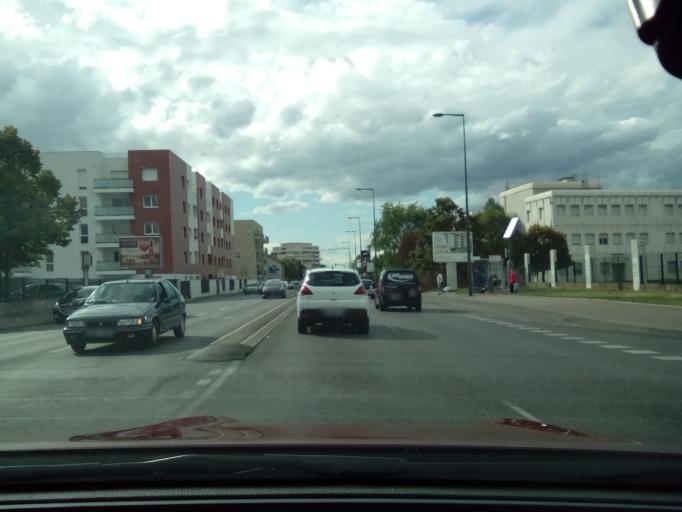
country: FR
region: Rhone-Alpes
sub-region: Departement du Rhone
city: Bron
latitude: 45.7451
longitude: 4.9299
